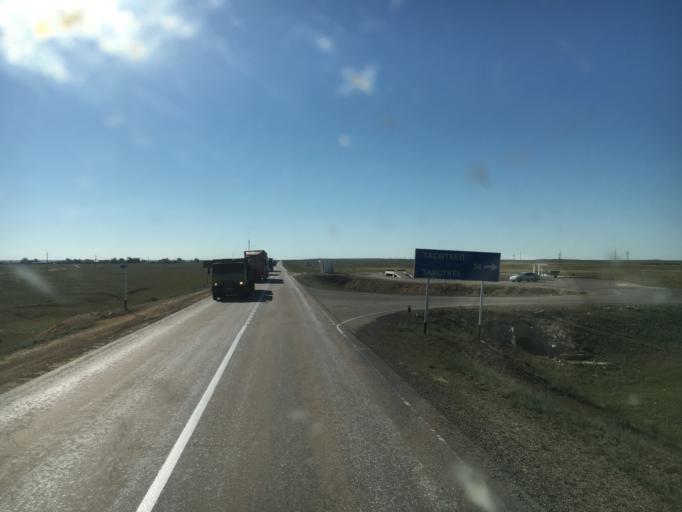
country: RU
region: Orenburg
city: Dombarovskiy
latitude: 50.0705
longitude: 59.6255
